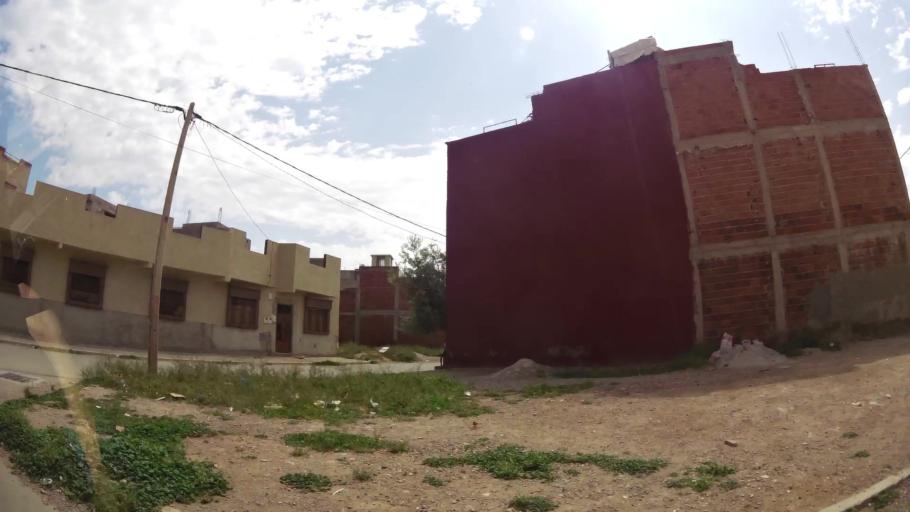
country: MA
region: Oriental
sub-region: Oujda-Angad
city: Oujda
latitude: 34.6824
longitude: -1.8986
